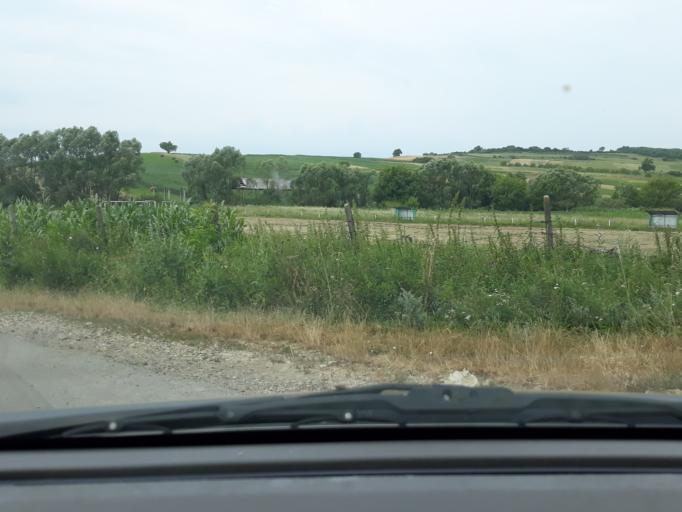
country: RO
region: Salaj
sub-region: Comuna Dobrin
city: Dobrin
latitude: 47.2890
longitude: 23.0953
